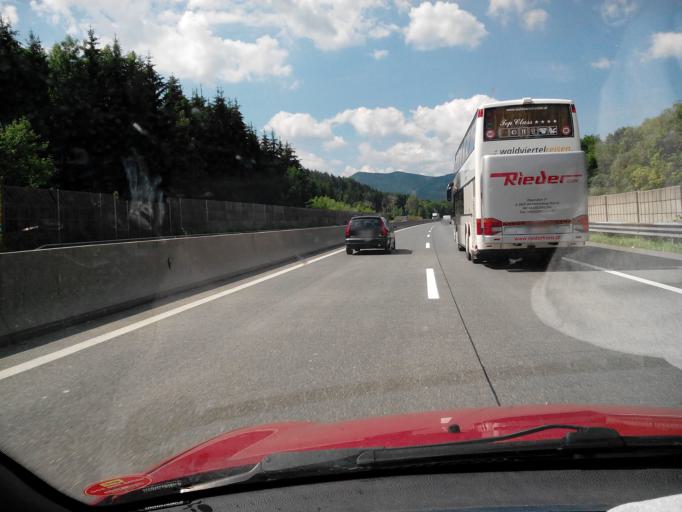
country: AT
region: Upper Austria
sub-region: Politischer Bezirk Vocklabruck
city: Oberwang
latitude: 47.8982
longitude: 13.4436
